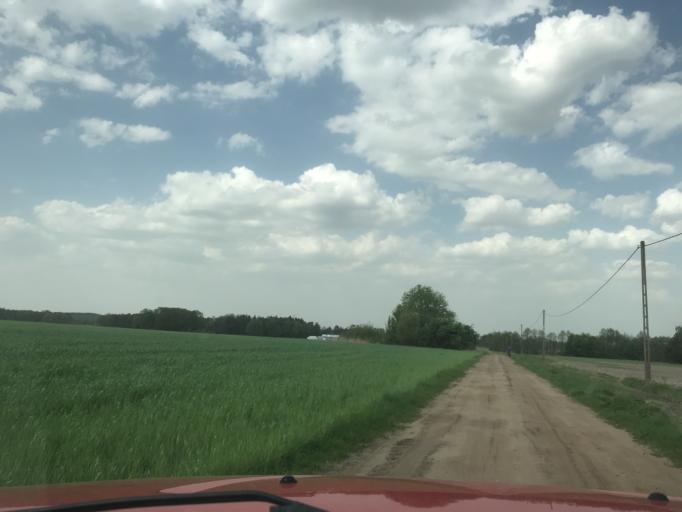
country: PL
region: Greater Poland Voivodeship
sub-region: Powiat turecki
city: Tuliszkow
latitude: 51.9563
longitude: 18.2577
